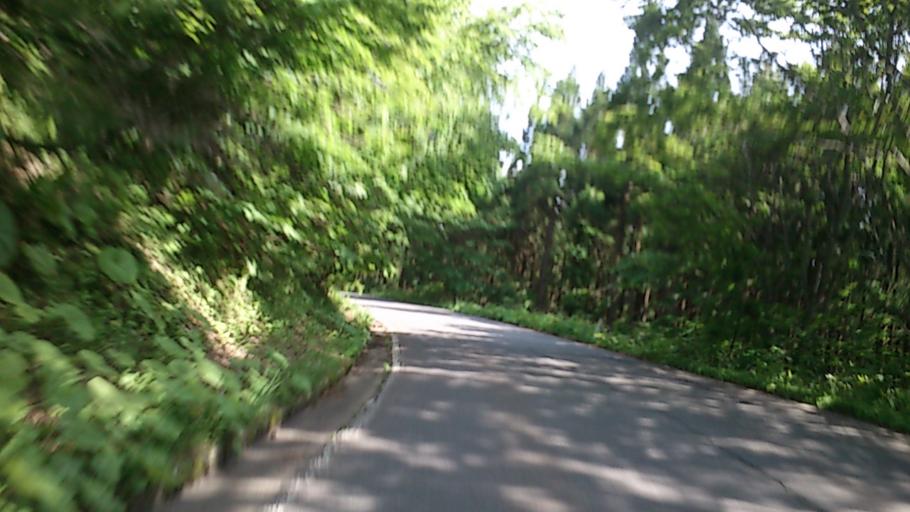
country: JP
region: Aomori
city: Aomori Shi
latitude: 40.7190
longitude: 140.8090
